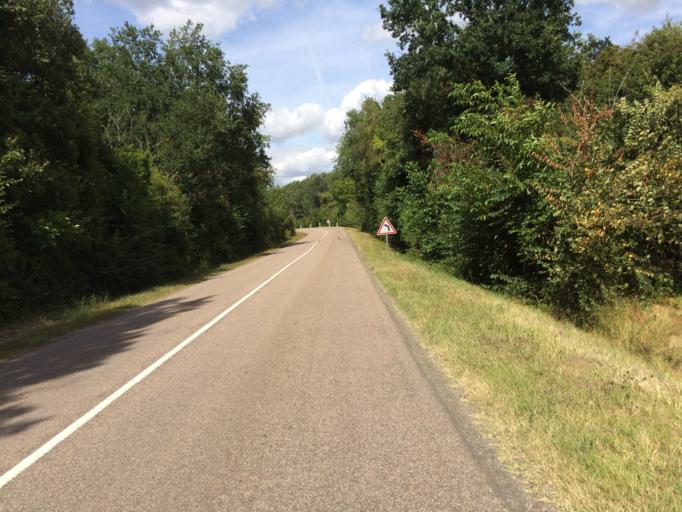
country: FR
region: Ile-de-France
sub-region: Departement de l'Essonne
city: Maisse
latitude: 48.3488
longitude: 2.3806
